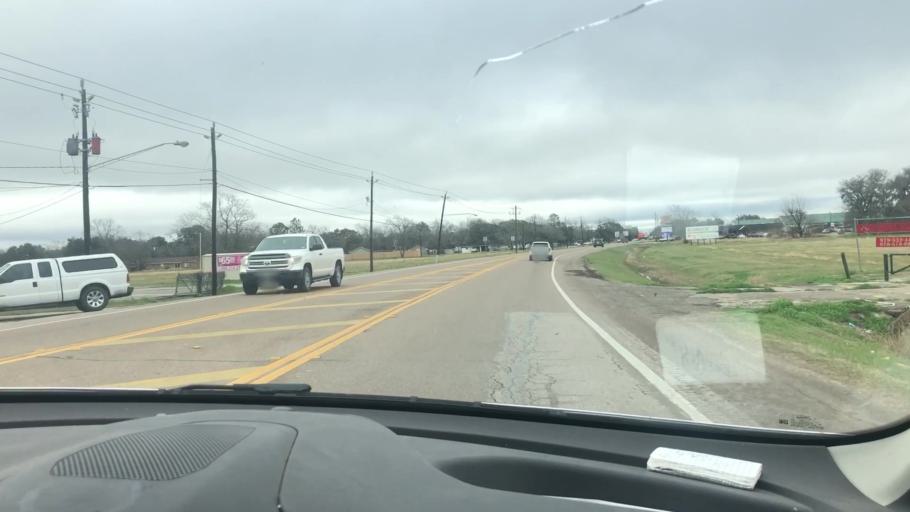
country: US
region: Texas
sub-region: Wharton County
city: Wharton
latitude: 29.3080
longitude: -96.0893
